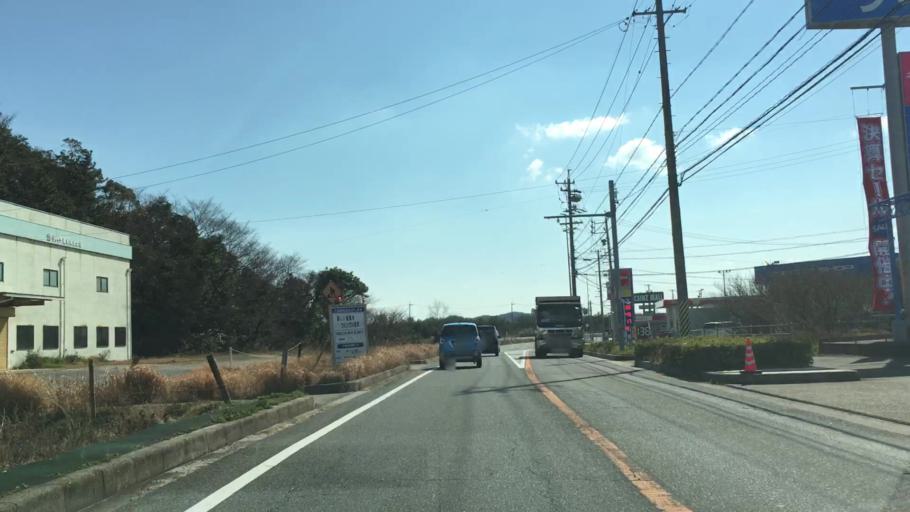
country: JP
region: Aichi
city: Gamagori
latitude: 34.8133
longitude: 137.1985
